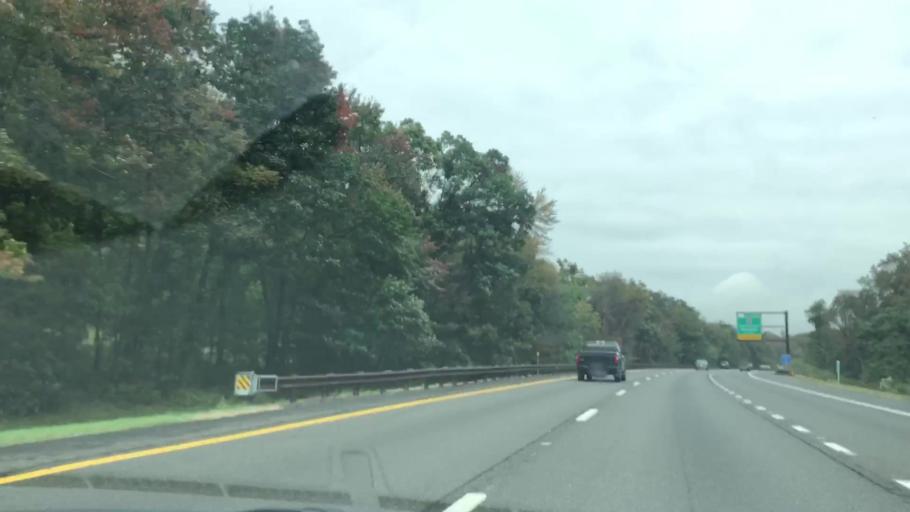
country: US
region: New Jersey
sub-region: Bergen County
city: Ho-Ho-Kus
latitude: 40.9887
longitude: -74.0727
